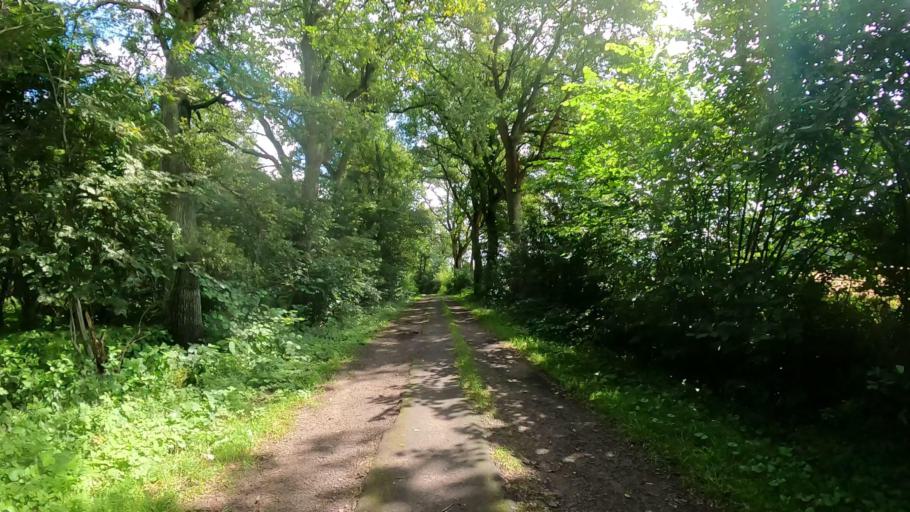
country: DE
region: Schleswig-Holstein
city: Bonningstedt
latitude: 53.6608
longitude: 9.9450
